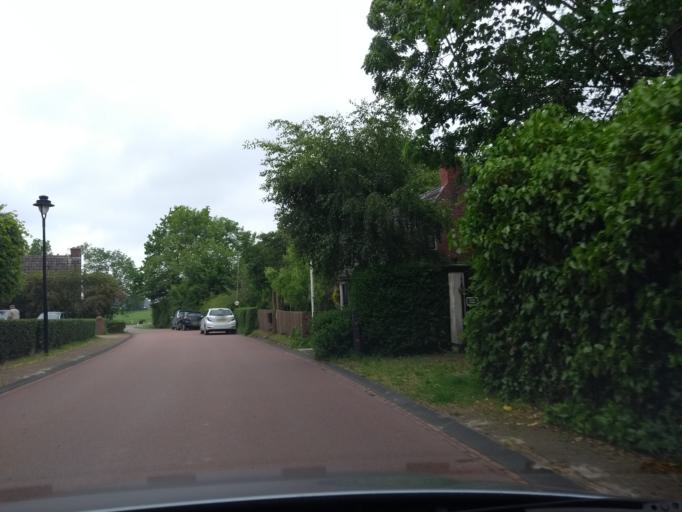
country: NL
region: Groningen
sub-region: Gemeente Zuidhorn
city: Oldehove
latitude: 53.3429
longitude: 6.4252
